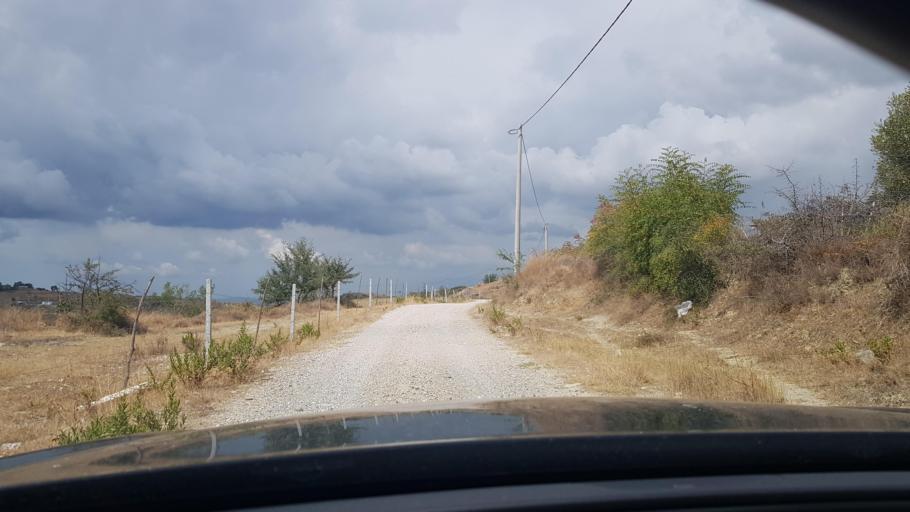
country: AL
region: Tirane
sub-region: Rrethi i Kavajes
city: Golem
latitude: 41.2852
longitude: 19.5473
